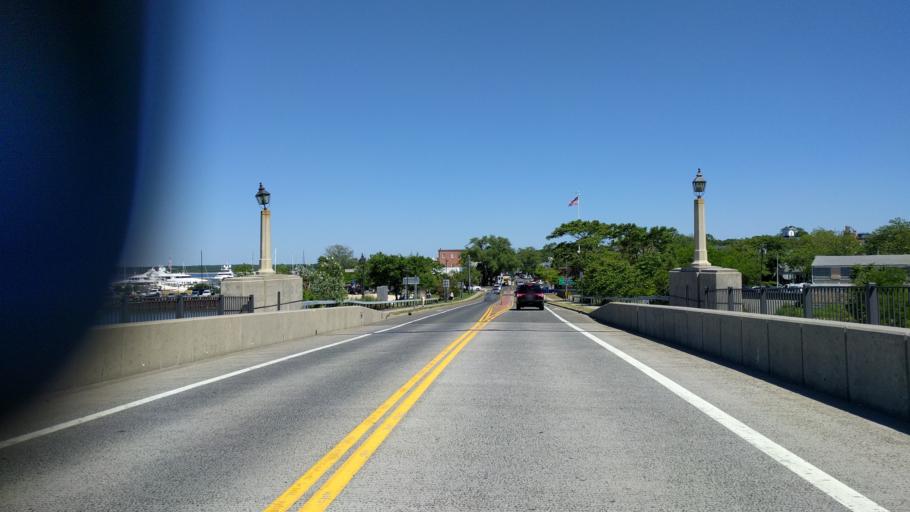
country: US
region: New York
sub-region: Suffolk County
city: Sag Harbor
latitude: 41.0032
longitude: -72.2982
